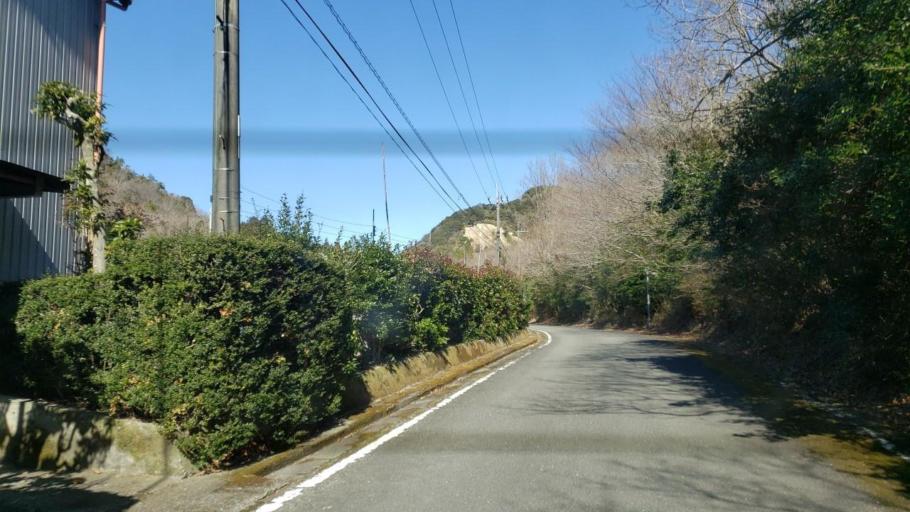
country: JP
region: Tokushima
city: Narutocho-mitsuishi
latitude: 34.1891
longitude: 134.5523
